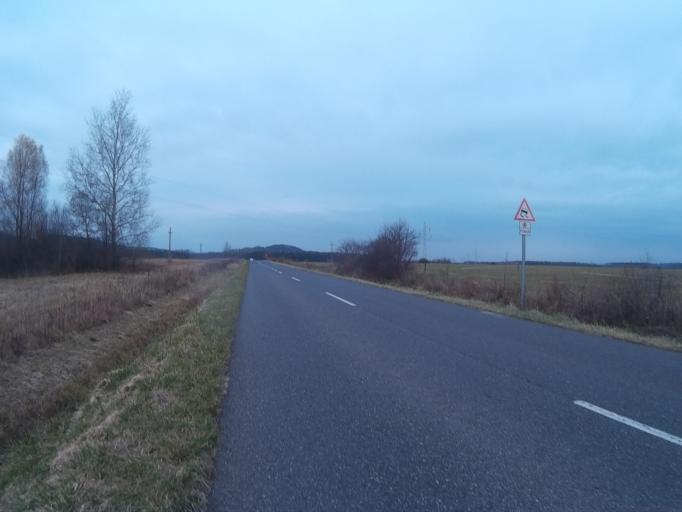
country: HU
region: Veszprem
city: Devecser
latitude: 46.9938
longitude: 17.4574
